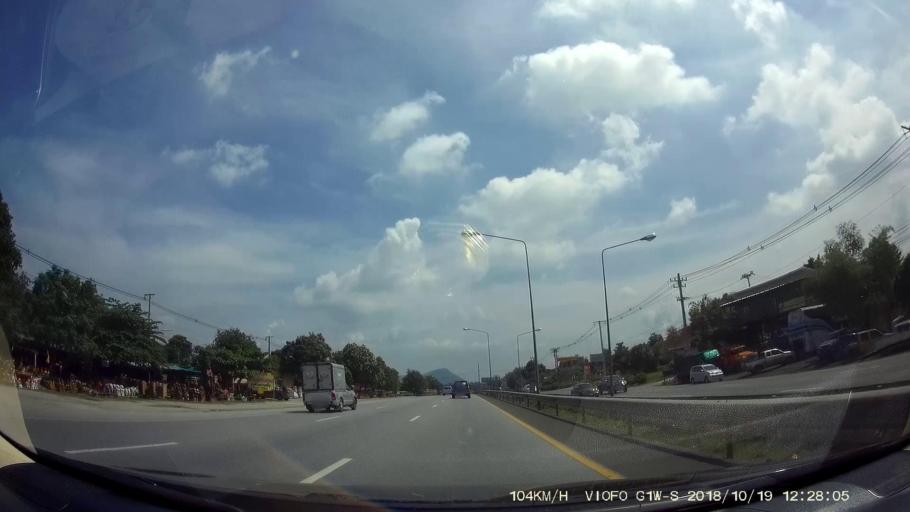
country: TH
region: Nakhon Ratchasima
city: Amphoe Sikhiu
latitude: 14.8446
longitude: 101.5898
